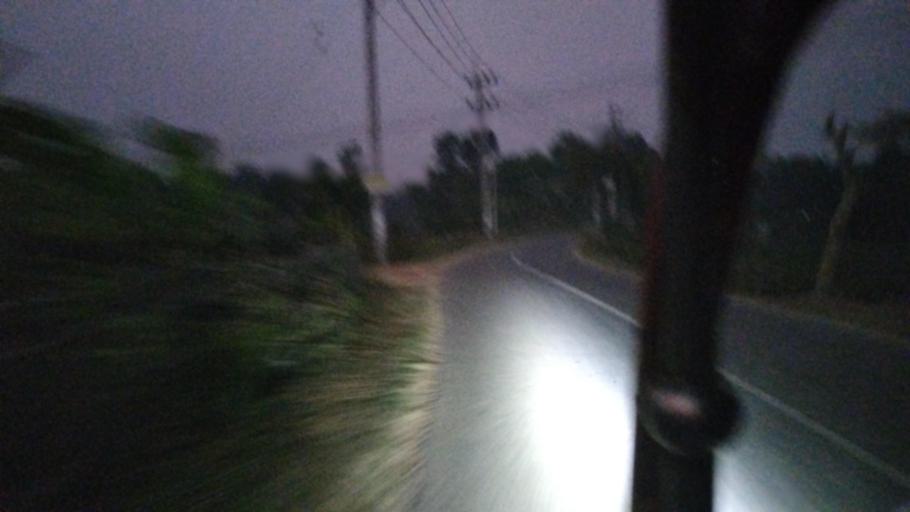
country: BD
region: Dhaka
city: Sakhipur
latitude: 24.4000
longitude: 90.3489
